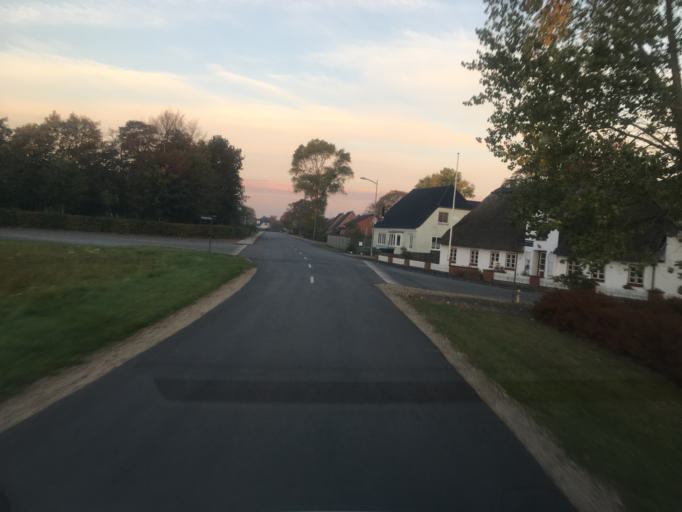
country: DK
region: South Denmark
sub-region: Tonder Kommune
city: Logumkloster
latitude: 54.9995
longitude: 9.0426
